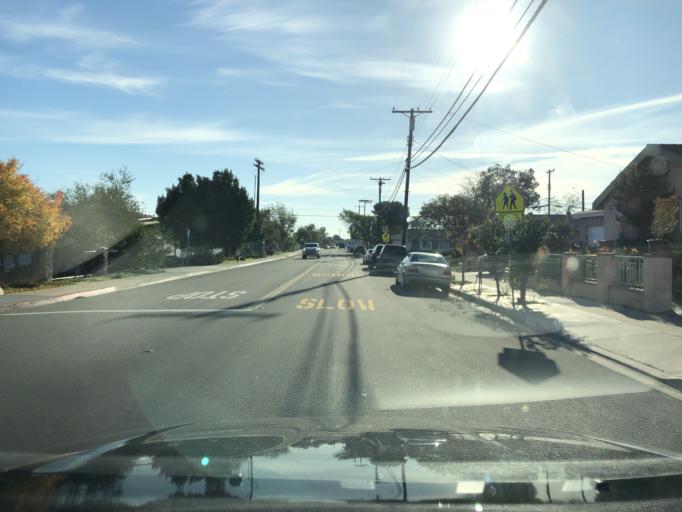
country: US
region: California
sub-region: San Diego County
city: La Jolla
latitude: 32.8242
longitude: -117.1937
